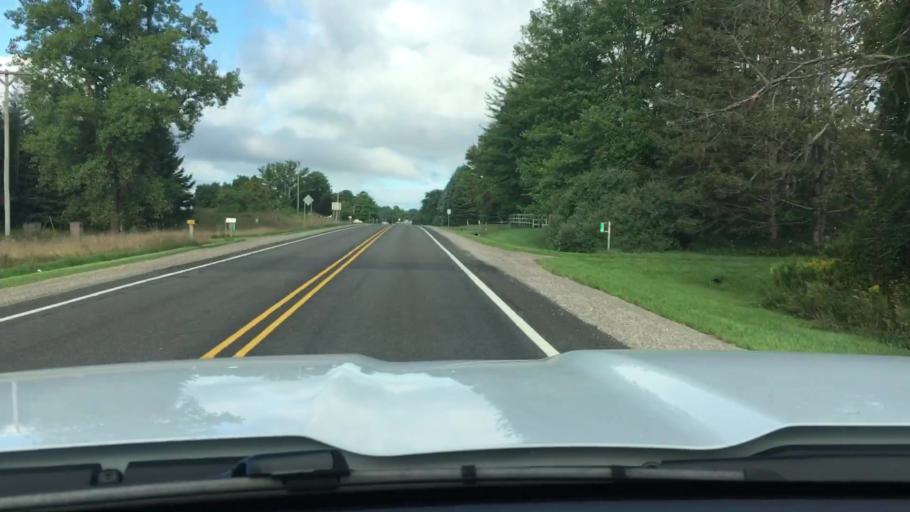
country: US
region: Michigan
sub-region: Lapeer County
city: Barnes Lake-Millers Lake
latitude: 43.3371
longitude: -83.3292
